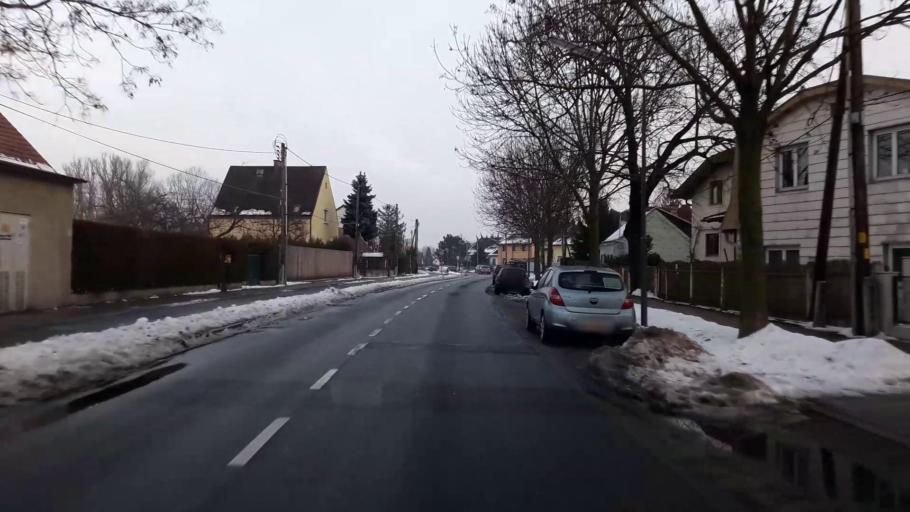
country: AT
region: Vienna
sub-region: Wien Stadt
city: Vienna
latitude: 48.2470
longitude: 16.4034
